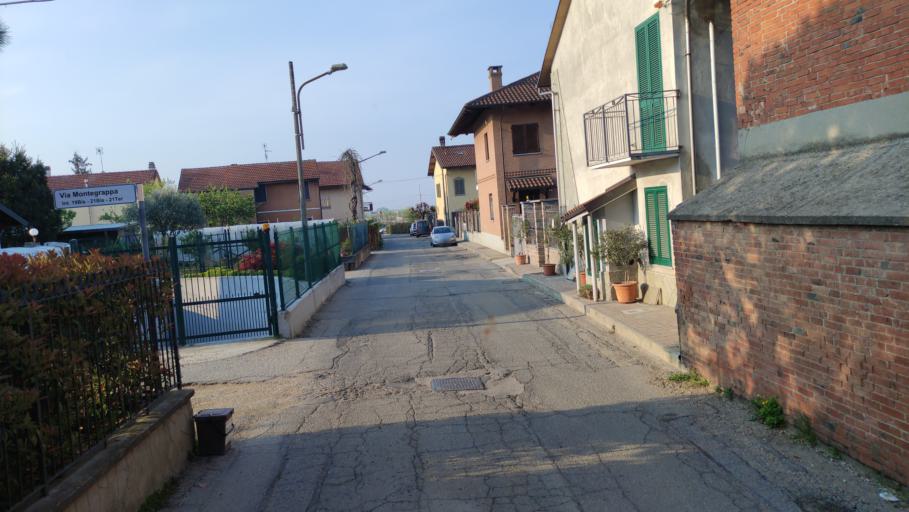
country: IT
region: Piedmont
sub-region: Provincia di Torino
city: Trofarello
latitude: 44.9841
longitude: 7.7310
